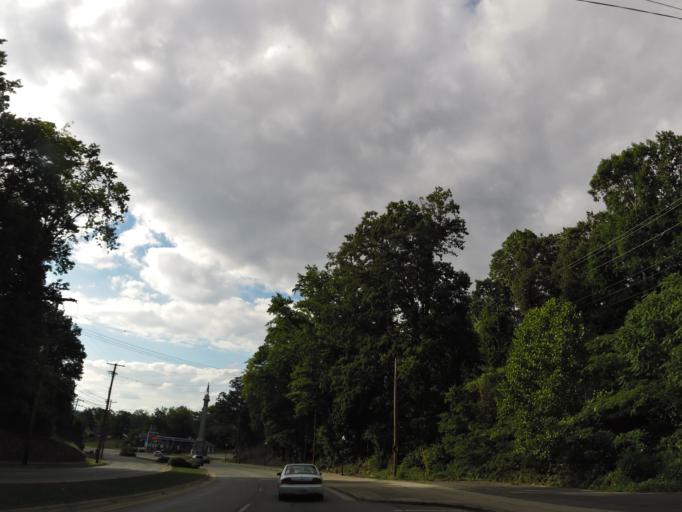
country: US
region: Georgia
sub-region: Walker County
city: Rossville
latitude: 34.9826
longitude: -85.2785
